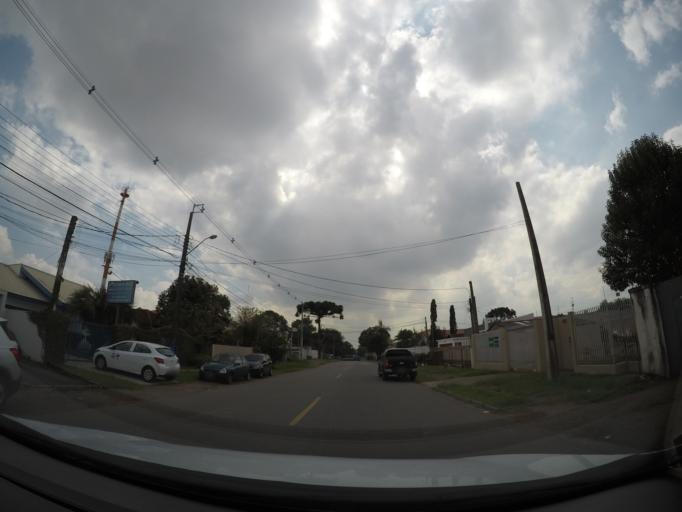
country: BR
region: Parana
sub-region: Sao Jose Dos Pinhais
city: Sao Jose dos Pinhais
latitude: -25.4997
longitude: -49.2410
